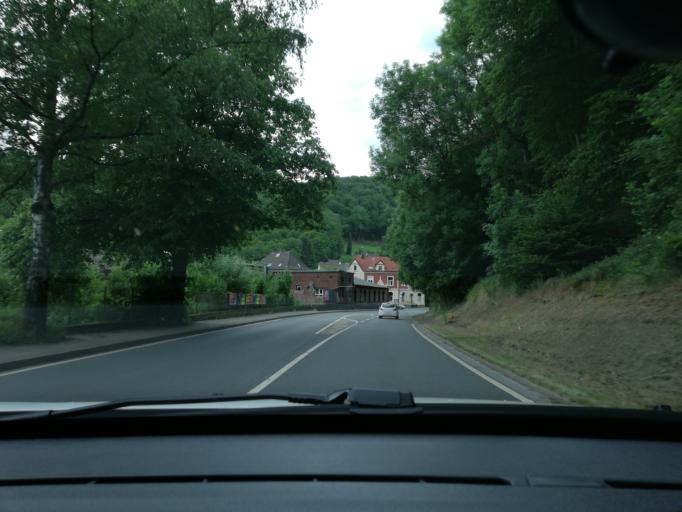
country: DE
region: North Rhine-Westphalia
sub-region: Regierungsbezirk Arnsberg
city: Schalksmuhle
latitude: 51.2866
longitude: 7.5212
